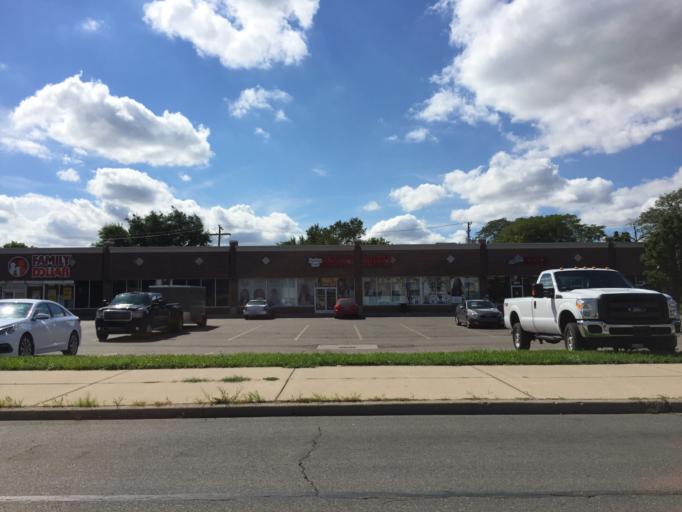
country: US
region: Michigan
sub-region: Wayne County
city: Highland Park
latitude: 42.3950
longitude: -83.0900
